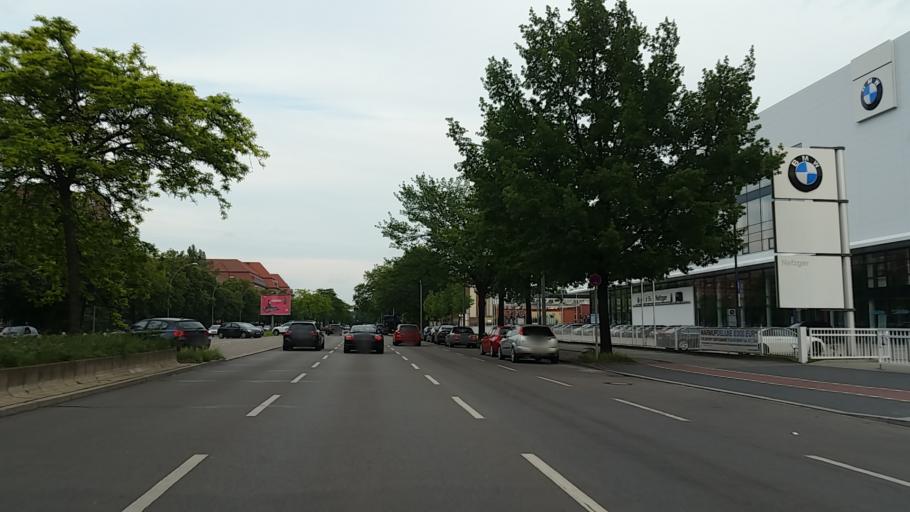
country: DE
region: Berlin
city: Siemensstadt
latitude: 52.5374
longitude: 13.2563
